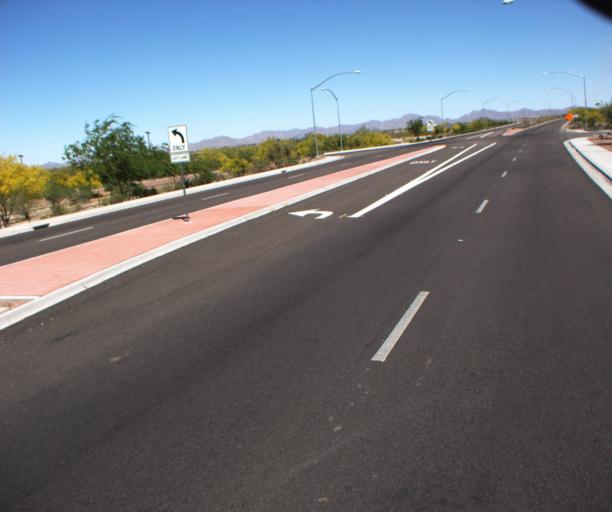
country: US
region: Arizona
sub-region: Maricopa County
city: Gila Bend
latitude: 32.9520
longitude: -112.6950
